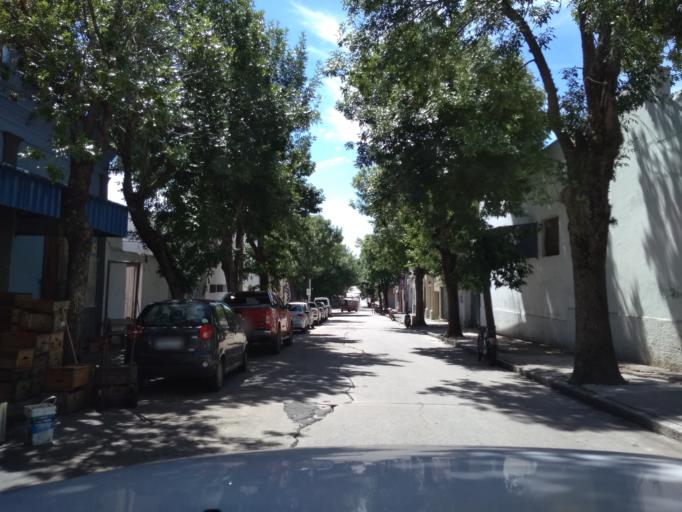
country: UY
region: Florida
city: Florida
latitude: -34.0996
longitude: -56.2157
